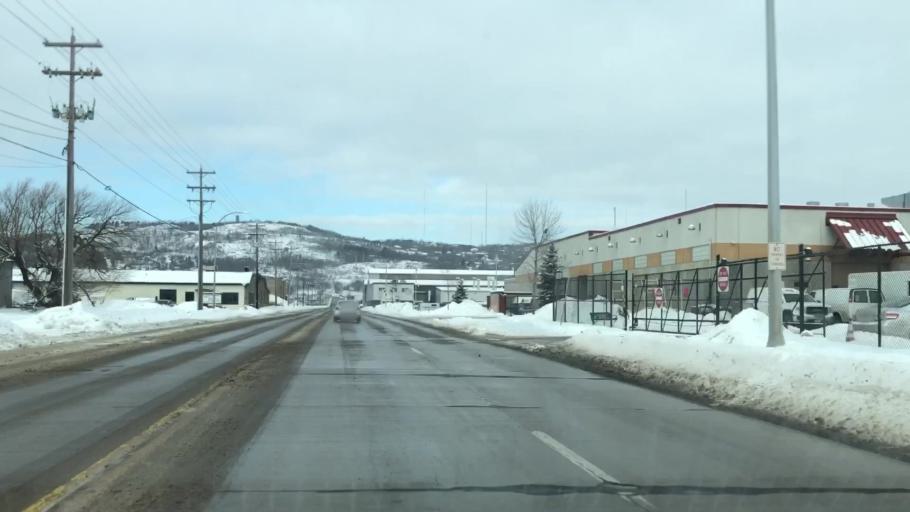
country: US
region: Minnesota
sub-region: Saint Louis County
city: Duluth
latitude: 46.7620
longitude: -92.1109
